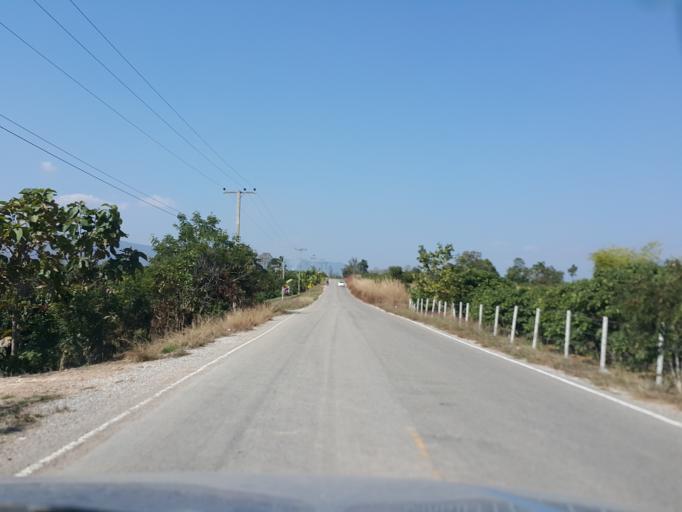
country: TH
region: Chiang Mai
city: Mae Wang
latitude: 18.5610
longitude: 98.7935
